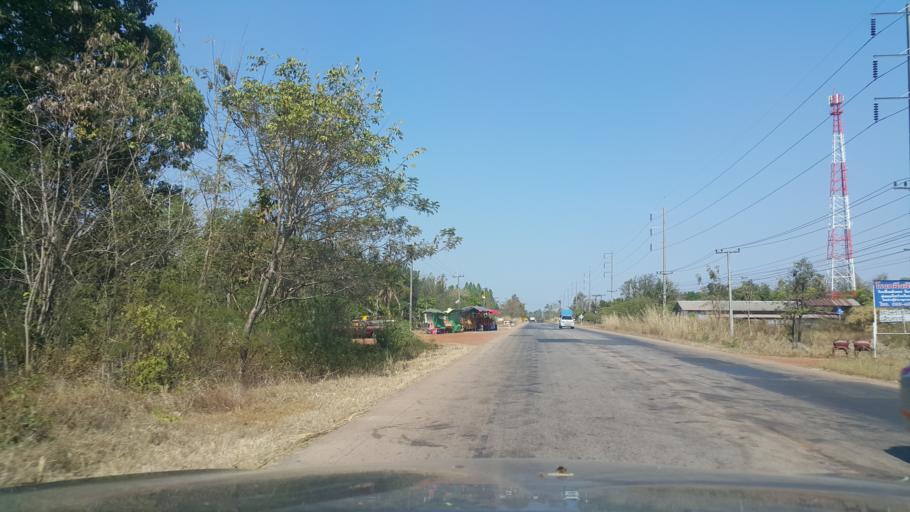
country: TH
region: Changwat Udon Thani
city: Ban Dung
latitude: 17.5895
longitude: 103.2462
